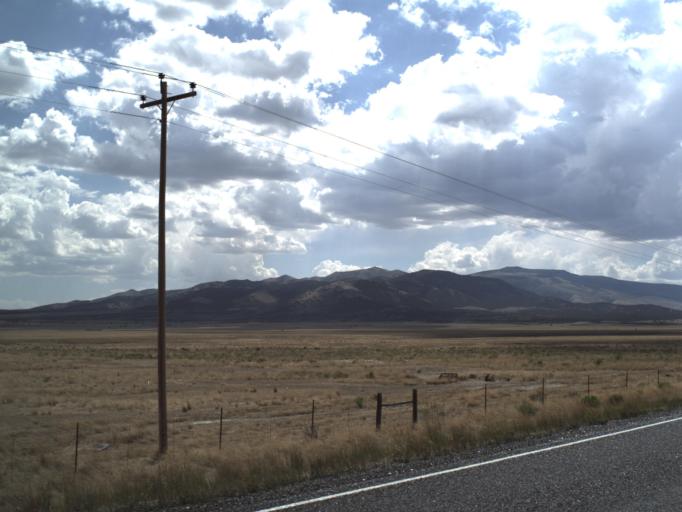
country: US
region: Idaho
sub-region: Power County
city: American Falls
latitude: 41.9692
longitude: -113.1095
